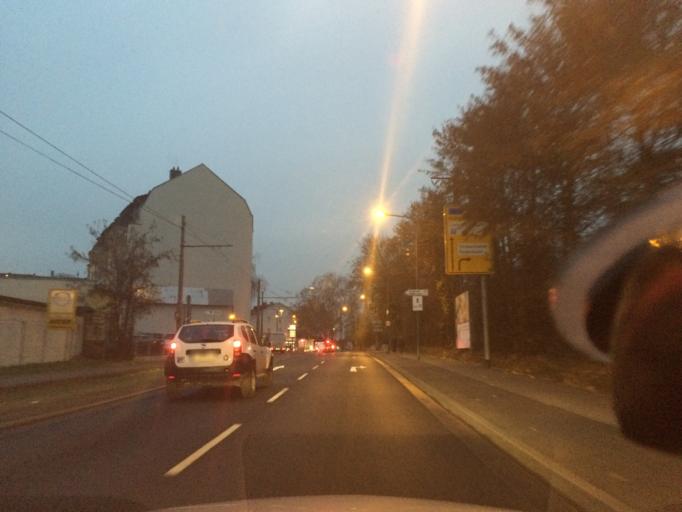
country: DE
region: Hesse
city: Sulzbach
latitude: 50.1032
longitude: 8.5543
